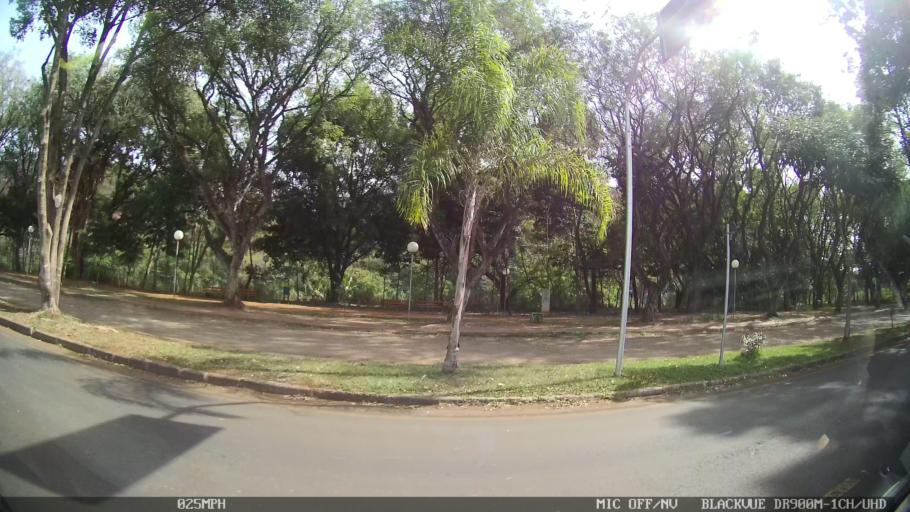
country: BR
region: Sao Paulo
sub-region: Piracicaba
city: Piracicaba
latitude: -22.7155
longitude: -47.6763
